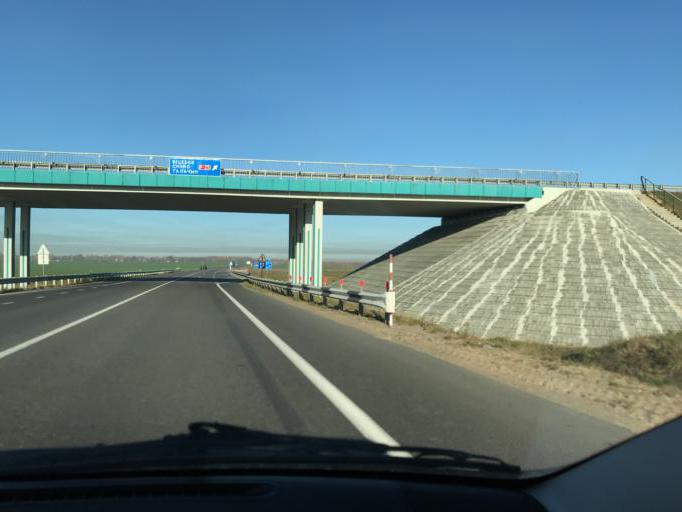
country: BY
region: Vitebsk
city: Vitebsk
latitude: 55.1099
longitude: 30.1055
